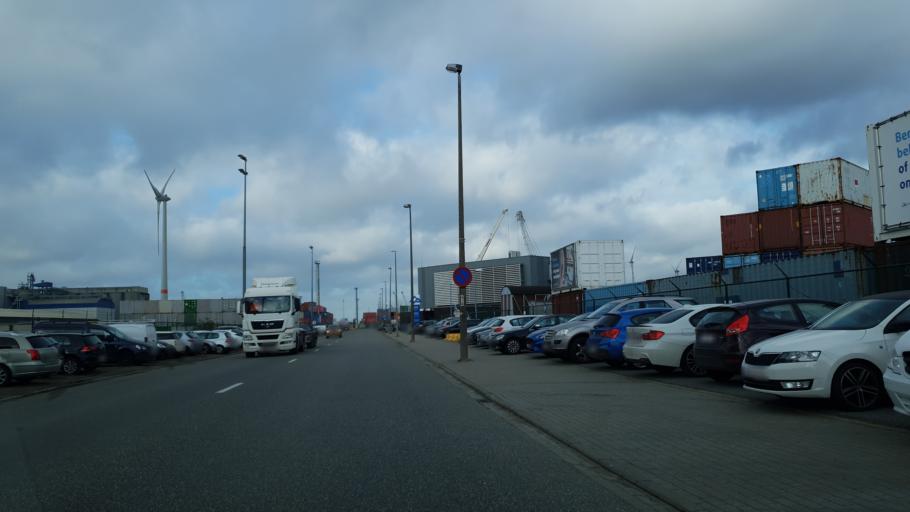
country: BE
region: Flanders
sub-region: Provincie Antwerpen
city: Stabroek
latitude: 51.2738
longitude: 4.3663
